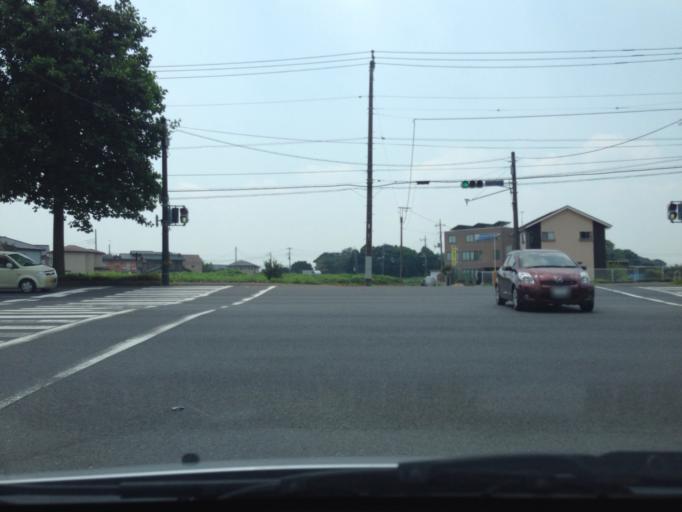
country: JP
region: Ibaraki
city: Naka
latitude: 36.0443
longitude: 140.1248
